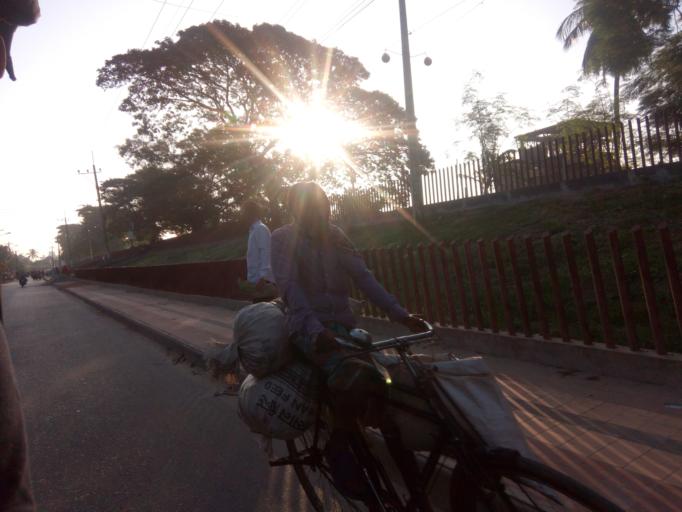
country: BD
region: Rajshahi
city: Rajshahi
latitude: 24.3615
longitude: 88.6116
